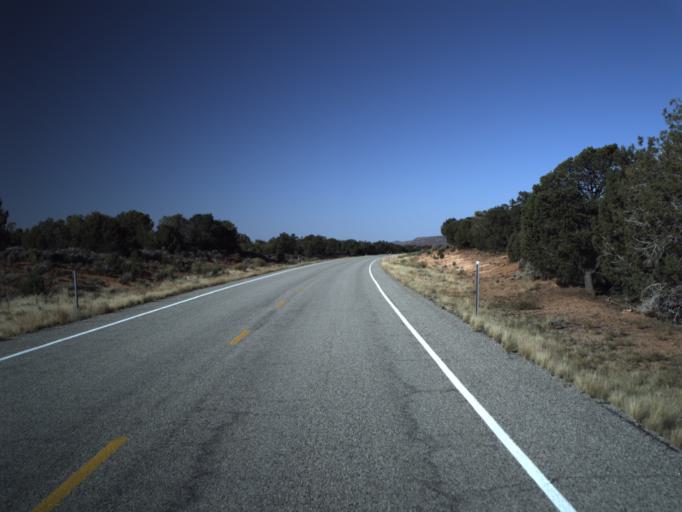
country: US
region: Utah
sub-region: San Juan County
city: Blanding
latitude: 37.5413
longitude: -109.9574
